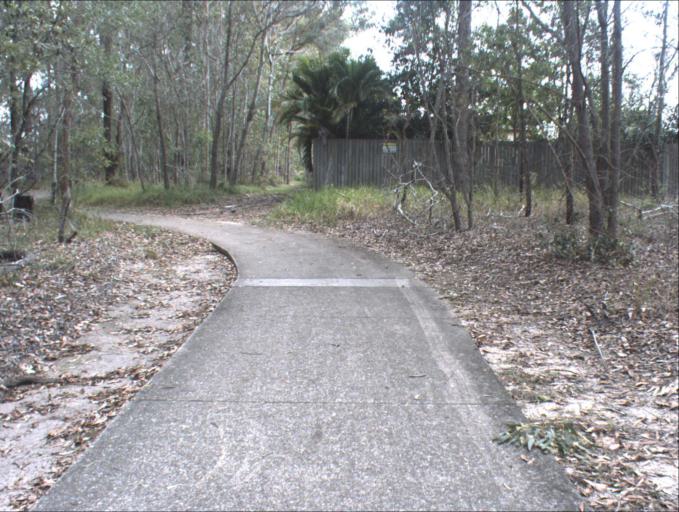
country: AU
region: Queensland
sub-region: Logan
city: Logan Reserve
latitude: -27.6883
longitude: 153.0656
